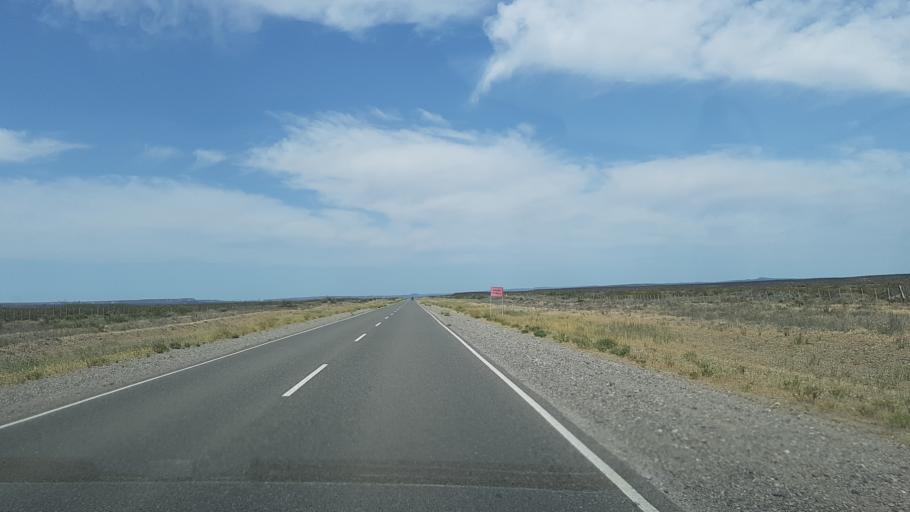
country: AR
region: Neuquen
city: Piedra del Aguila
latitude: -39.8260
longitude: -69.7466
